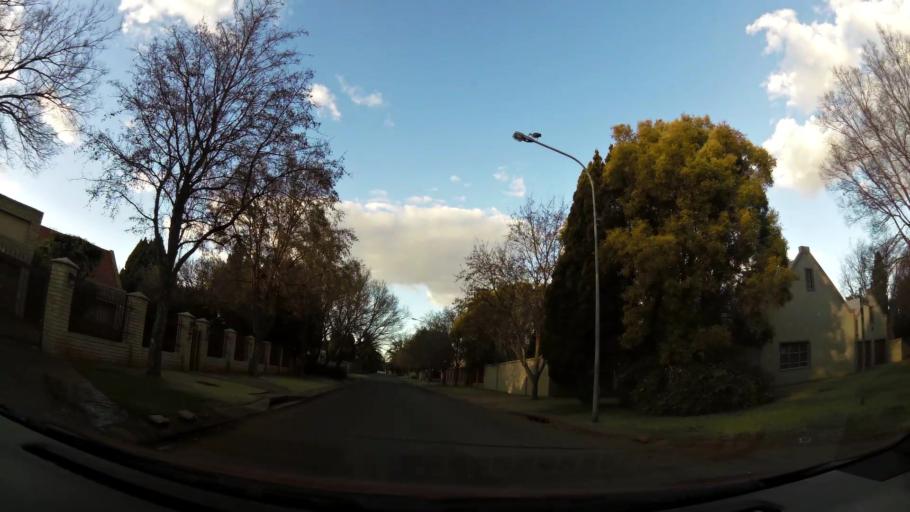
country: ZA
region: North-West
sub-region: Dr Kenneth Kaunda District Municipality
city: Potchefstroom
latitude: -26.6790
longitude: 27.1090
